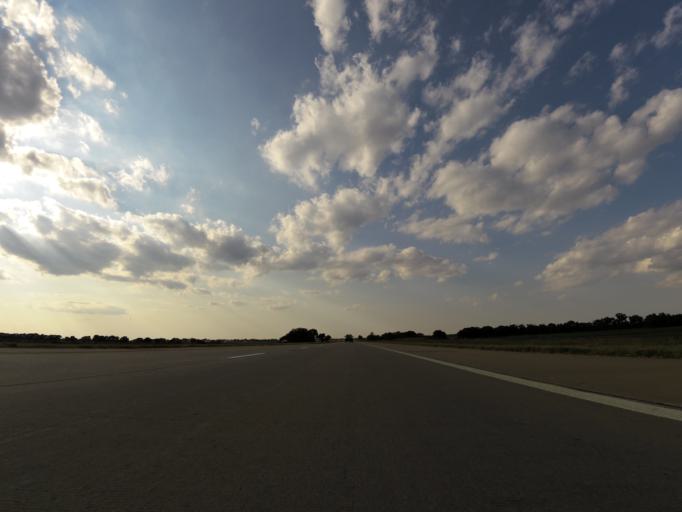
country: US
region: Kansas
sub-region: Sedgwick County
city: Colwich
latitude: 37.8623
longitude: -97.6182
